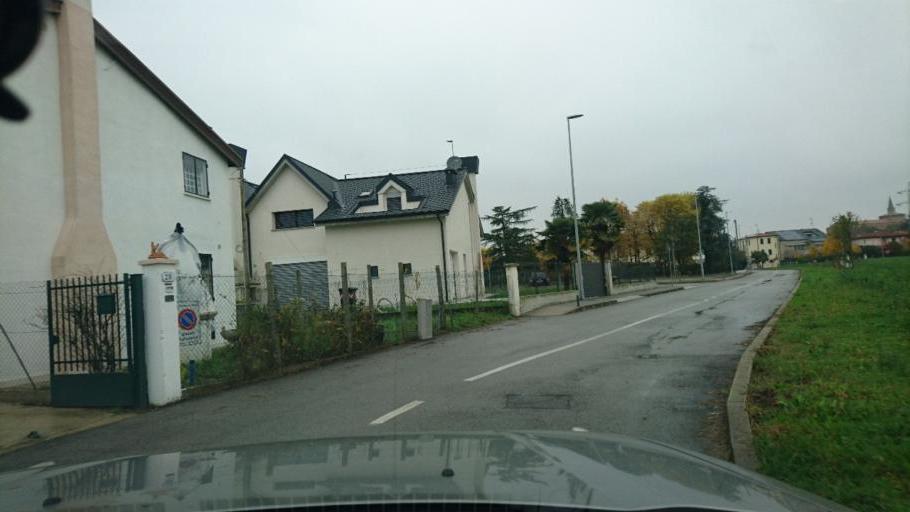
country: IT
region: Veneto
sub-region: Provincia di Padova
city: Padova
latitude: 45.4298
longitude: 11.8687
